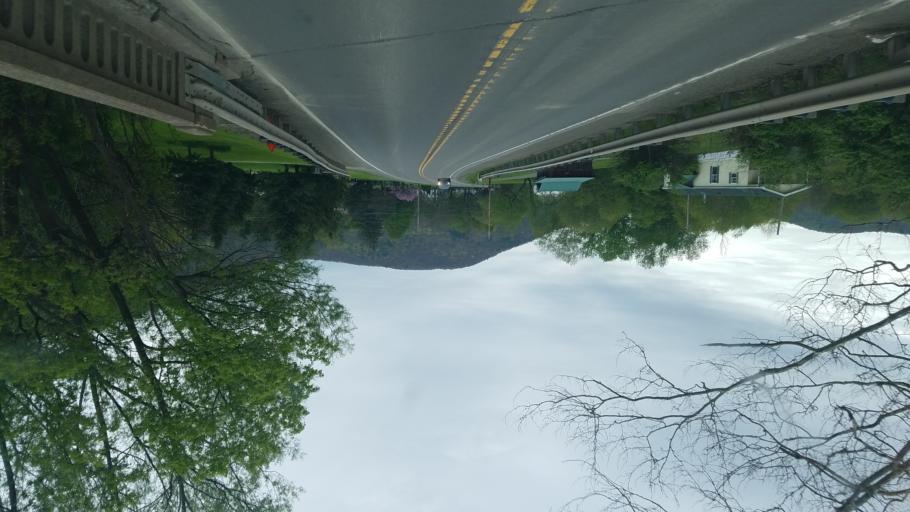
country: US
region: Pennsylvania
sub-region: Tioga County
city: Westfield
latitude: 41.9178
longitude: -77.5598
